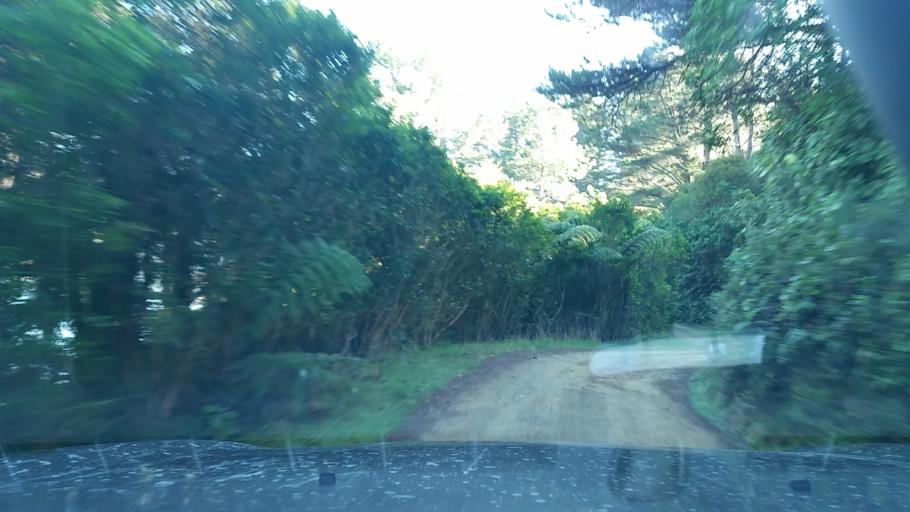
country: NZ
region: Marlborough
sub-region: Marlborough District
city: Picton
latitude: -41.1178
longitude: 173.9942
